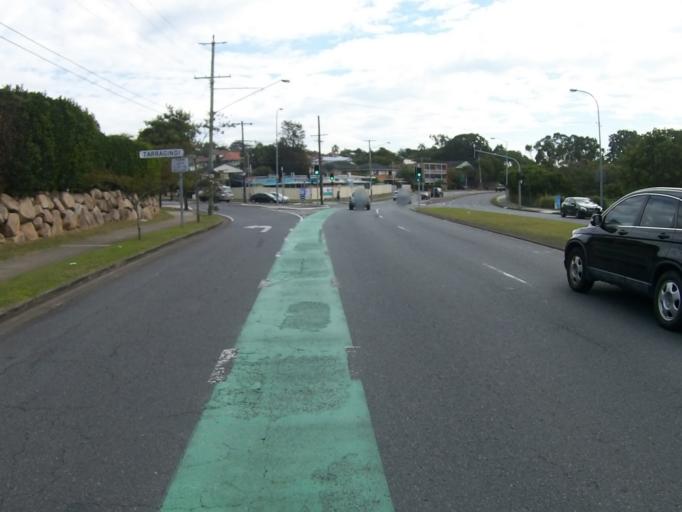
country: AU
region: Queensland
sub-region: Brisbane
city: Greenslopes
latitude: -27.5255
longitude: 153.0549
